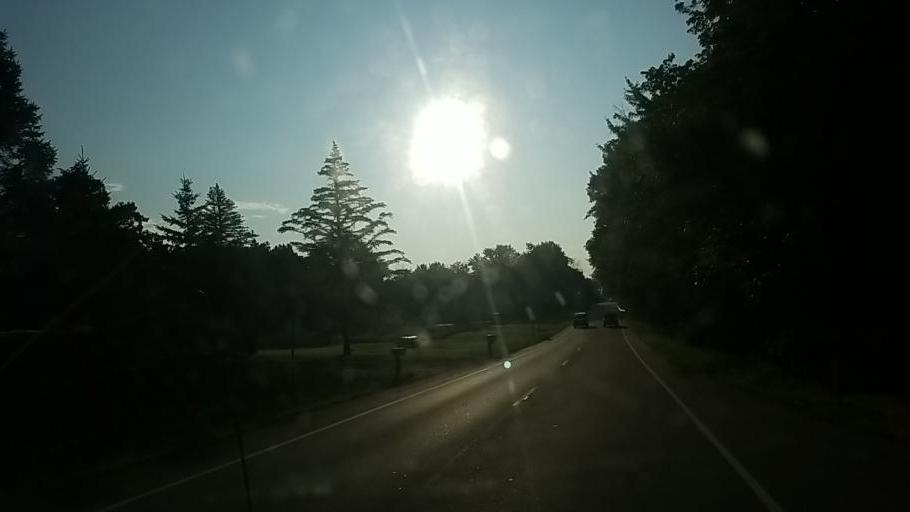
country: US
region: Michigan
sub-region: Montcalm County
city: Greenville
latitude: 43.2500
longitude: -85.3009
